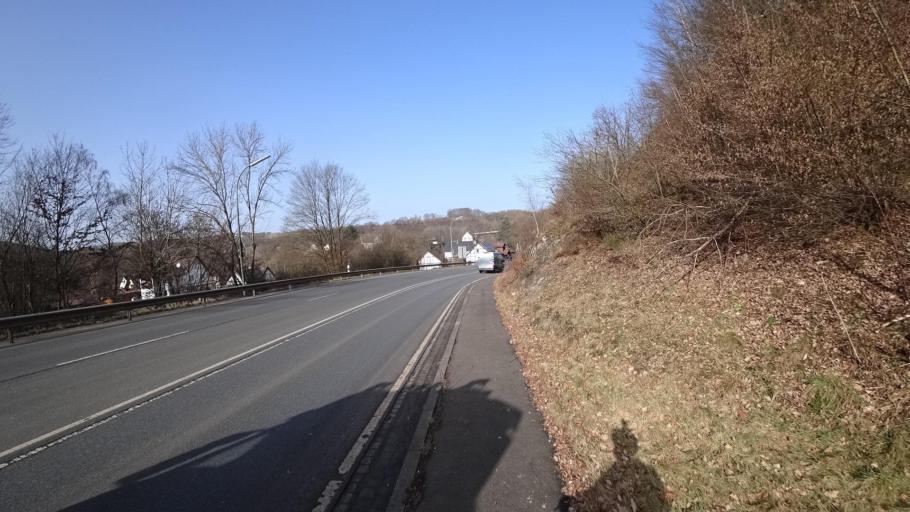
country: DE
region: Rheinland-Pfalz
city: Wissen
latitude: 50.7715
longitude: 7.7148
